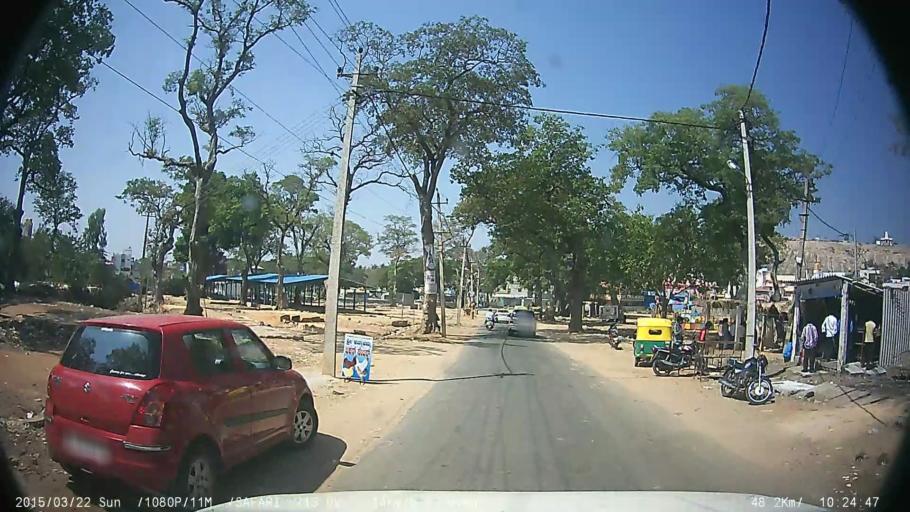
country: IN
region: Karnataka
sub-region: Bangalore Urban
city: Anekal
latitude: 12.8130
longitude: 77.5797
